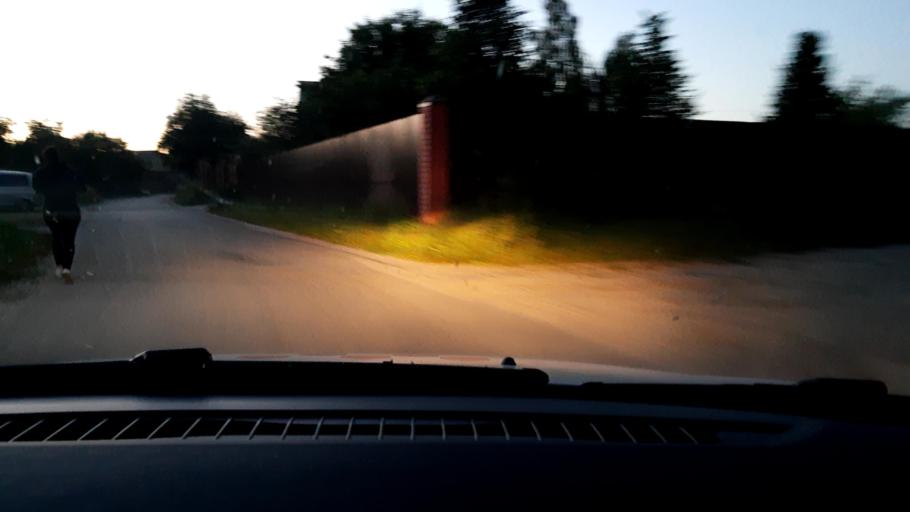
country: RU
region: Nizjnij Novgorod
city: Neklyudovo
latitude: 56.4182
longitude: 44.0209
